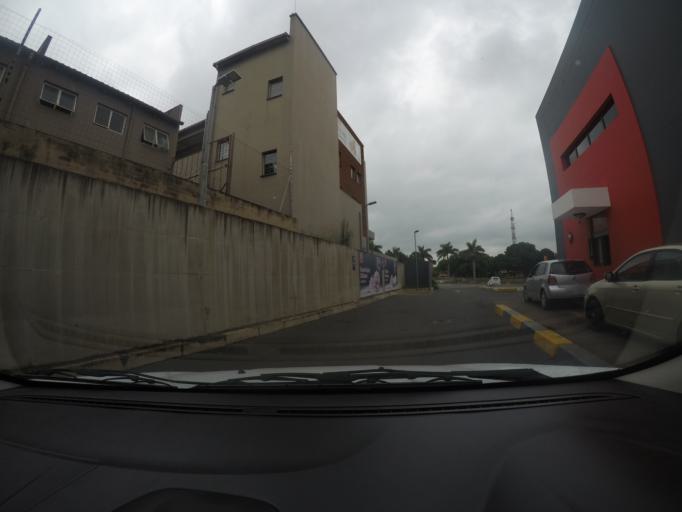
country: ZA
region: KwaZulu-Natal
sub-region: uThungulu District Municipality
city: Empangeni
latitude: -28.7464
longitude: 31.8899
